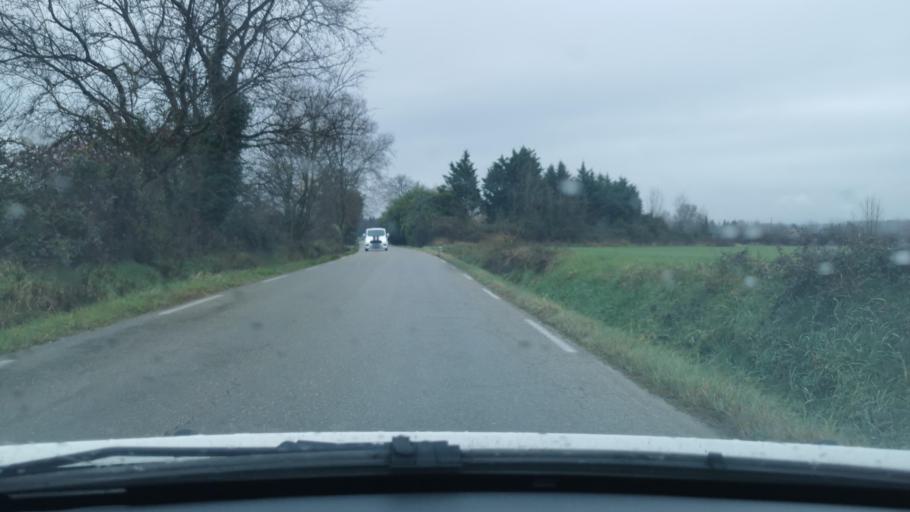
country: FR
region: Languedoc-Roussillon
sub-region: Departement du Gard
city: Saint-Quentin-la-Poterie
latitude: 44.0223
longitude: 4.4371
